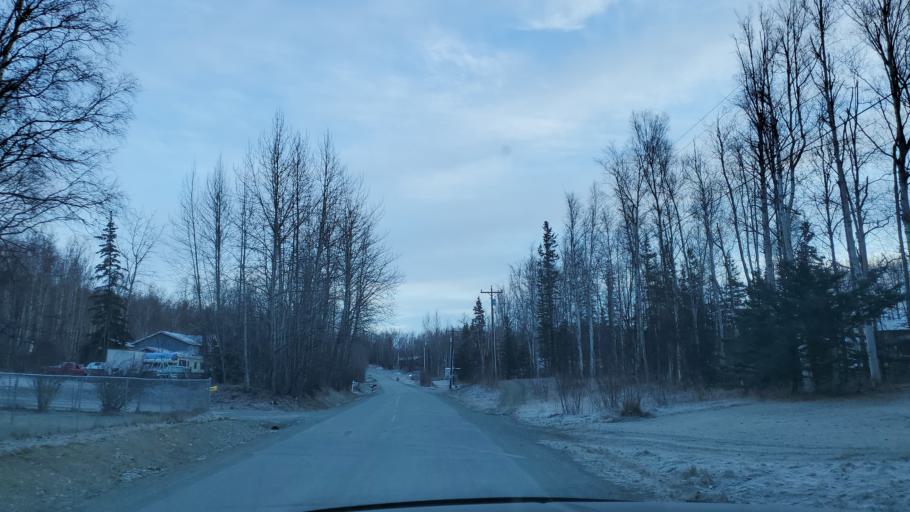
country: US
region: Alaska
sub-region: Matanuska-Susitna Borough
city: Lakes
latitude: 61.6035
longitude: -149.3213
